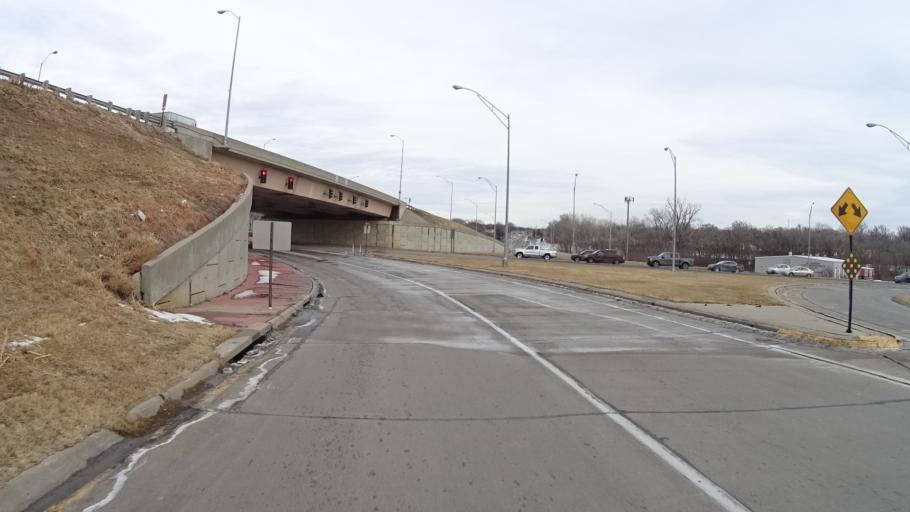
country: US
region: Nebraska
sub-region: Sarpy County
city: Offutt Air Force Base
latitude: 41.1398
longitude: -95.9274
